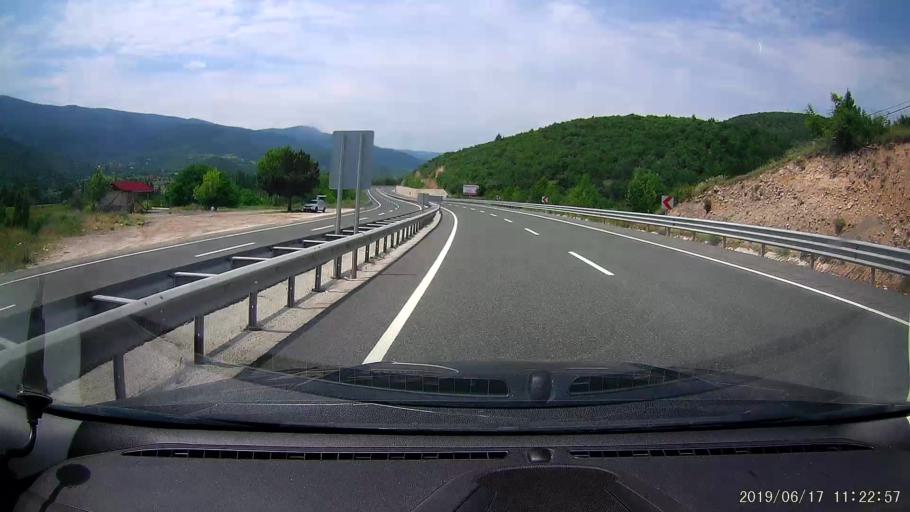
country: TR
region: Cankiri
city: Ilgaz
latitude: 40.8951
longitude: 33.7417
